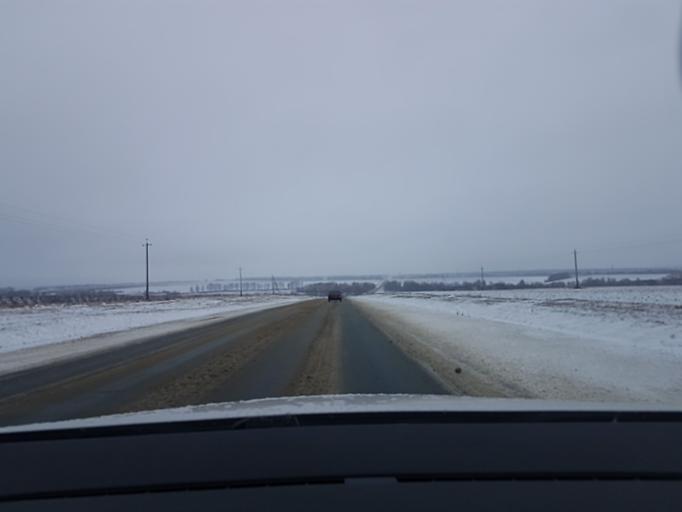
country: RU
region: Rjazan
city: Pavelets
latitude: 54.0473
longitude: 39.2848
